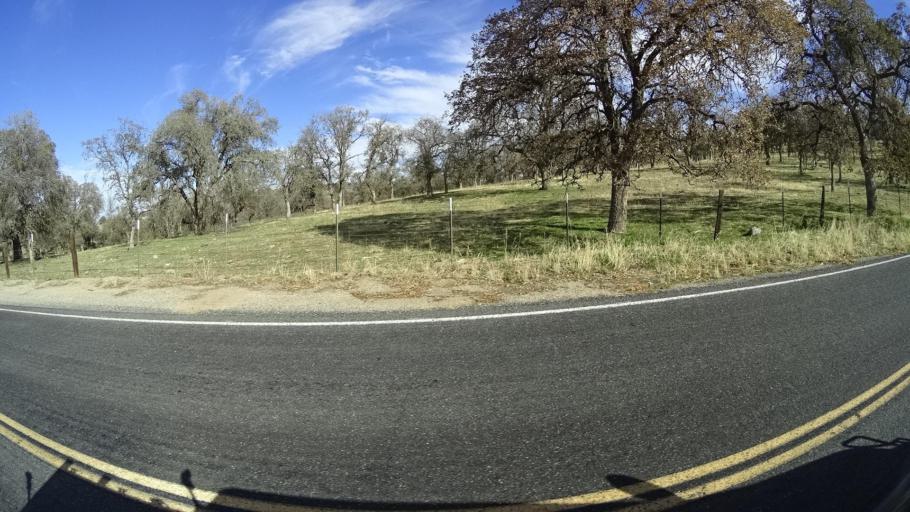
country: US
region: California
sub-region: Kern County
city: Alta Sierra
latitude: 35.6470
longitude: -118.7893
